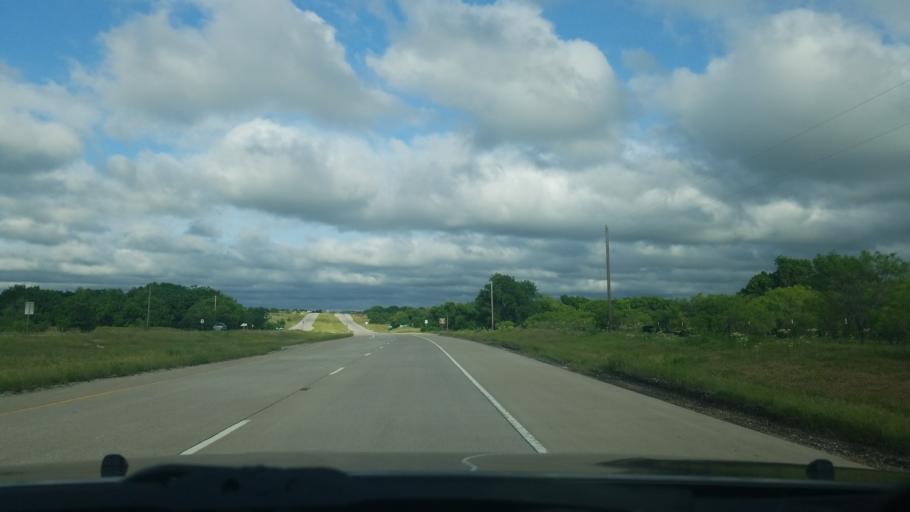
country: US
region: Texas
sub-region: Denton County
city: Ponder
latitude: 33.2463
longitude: -97.3934
